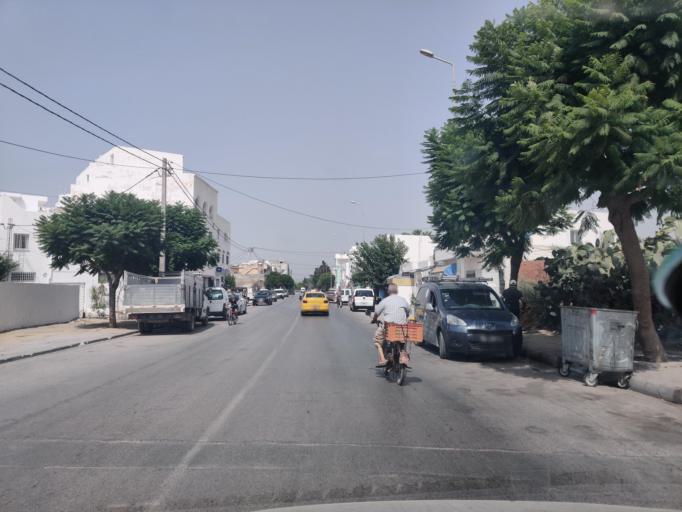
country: TN
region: Nabul
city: Al Hammamat
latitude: 36.4086
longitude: 10.6070
